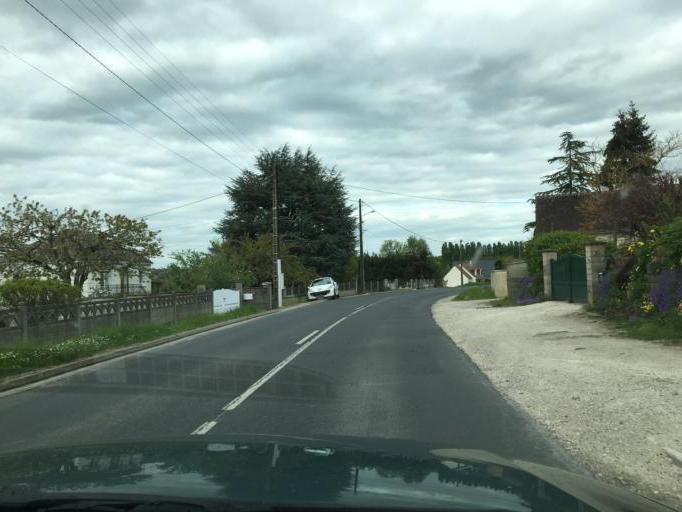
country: FR
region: Centre
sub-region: Departement du Loir-et-Cher
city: Saint-Ouen
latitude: 47.7946
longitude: 1.0945
